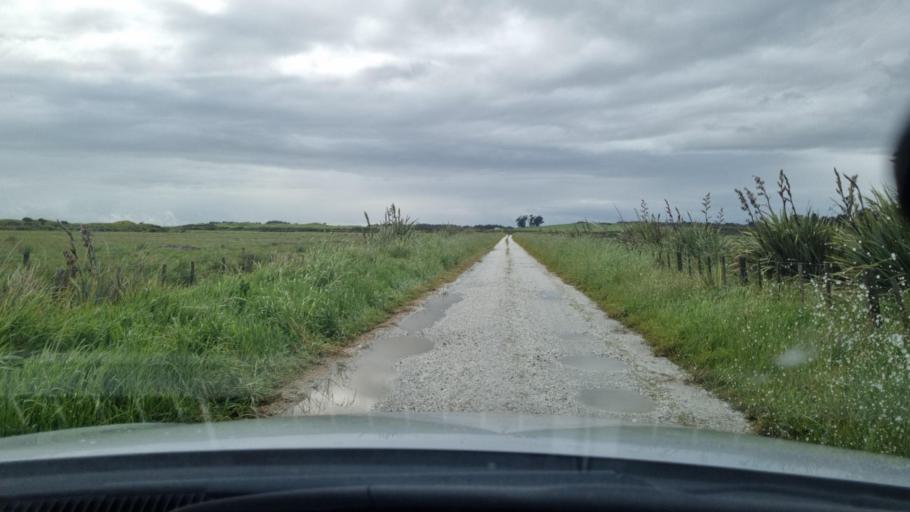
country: NZ
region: Southland
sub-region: Invercargill City
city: Bluff
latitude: -46.5201
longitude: 168.2765
